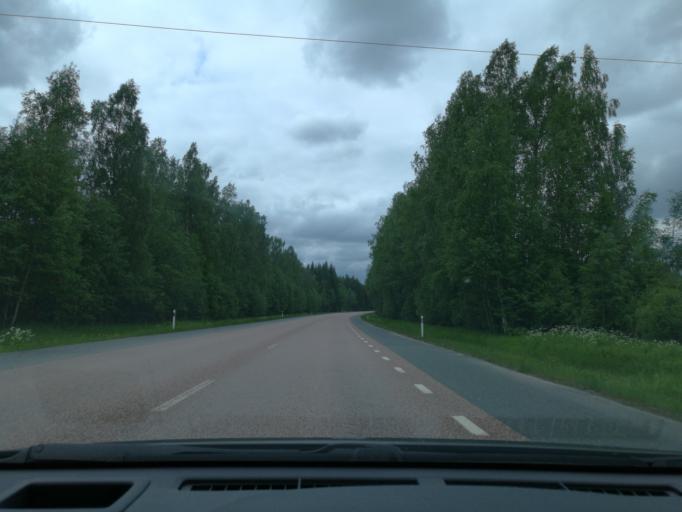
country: SE
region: Vaestmanland
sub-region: Fagersta Kommun
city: Fagersta
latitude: 59.9673
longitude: 15.7267
